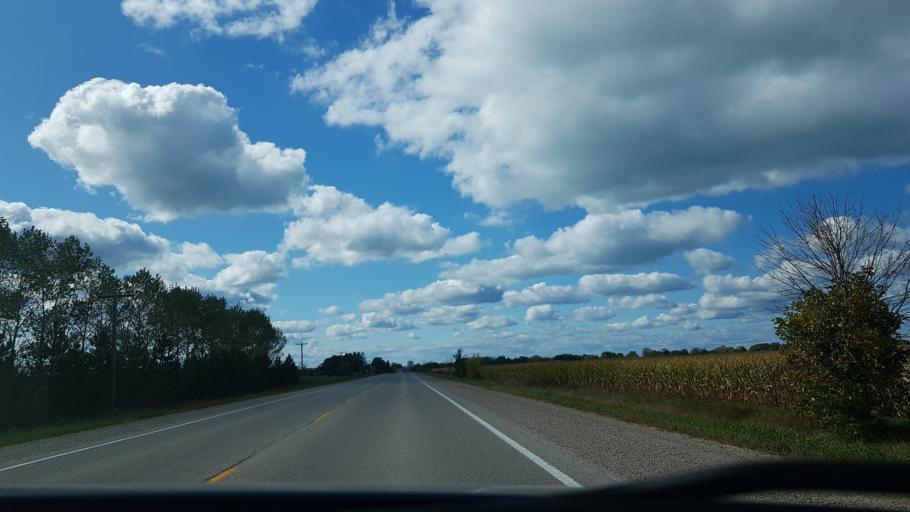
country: CA
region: Ontario
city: Bluewater
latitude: 43.3371
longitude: -81.7212
